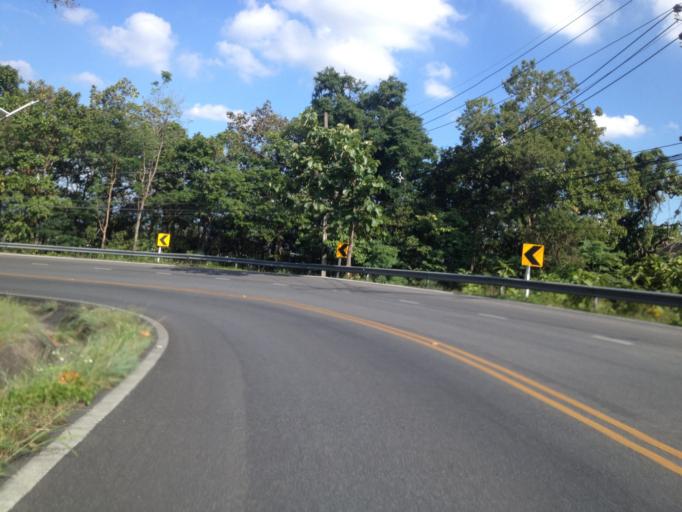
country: TH
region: Chiang Mai
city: Chiang Mai
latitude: 18.8113
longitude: 98.9377
